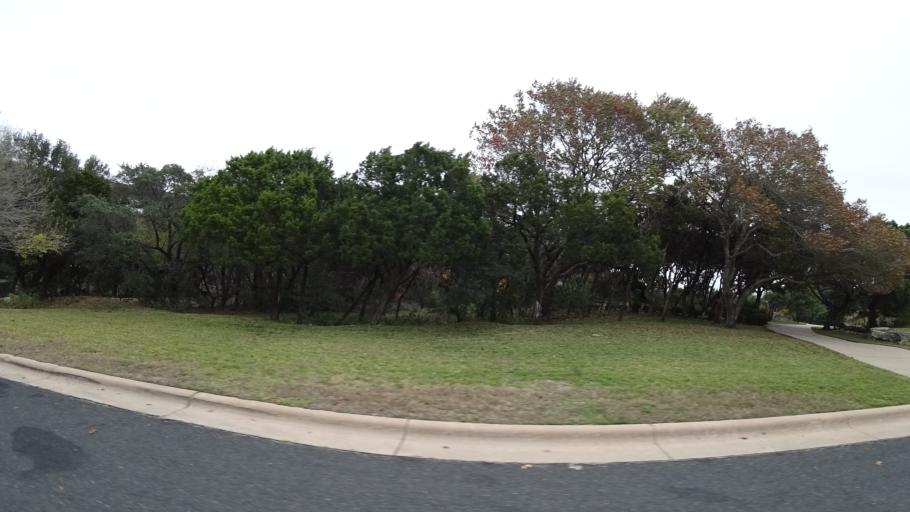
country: US
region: Texas
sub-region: Williamson County
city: Jollyville
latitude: 30.3765
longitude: -97.8120
